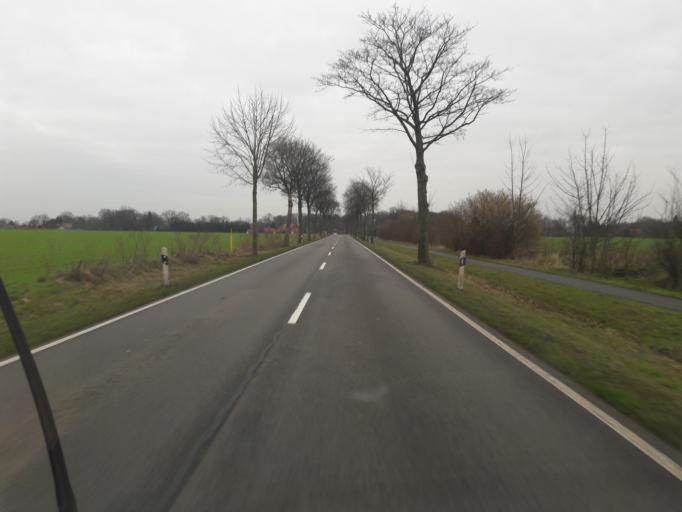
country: DE
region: Lower Saxony
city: Warmsen
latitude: 52.4772
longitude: 8.8744
